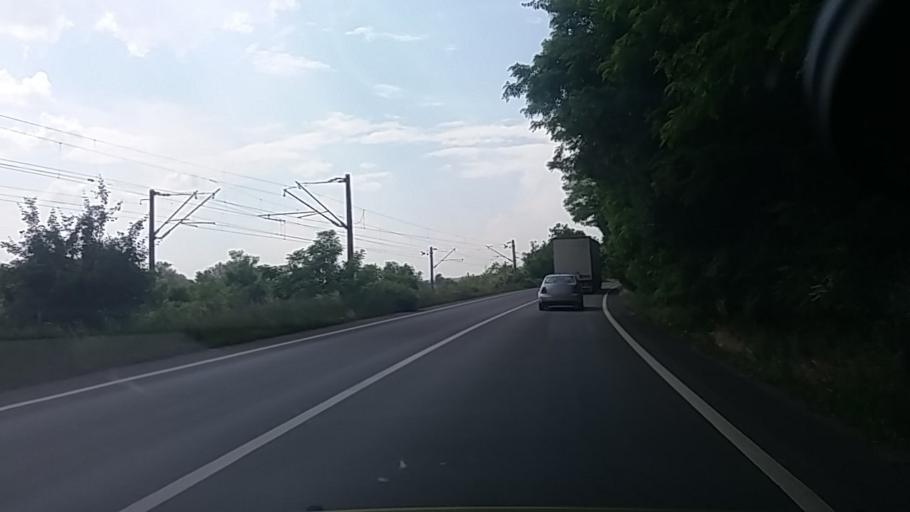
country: RO
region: Arad
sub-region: Comuna Savarsin
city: Savarsin
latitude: 45.9965
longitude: 22.2930
